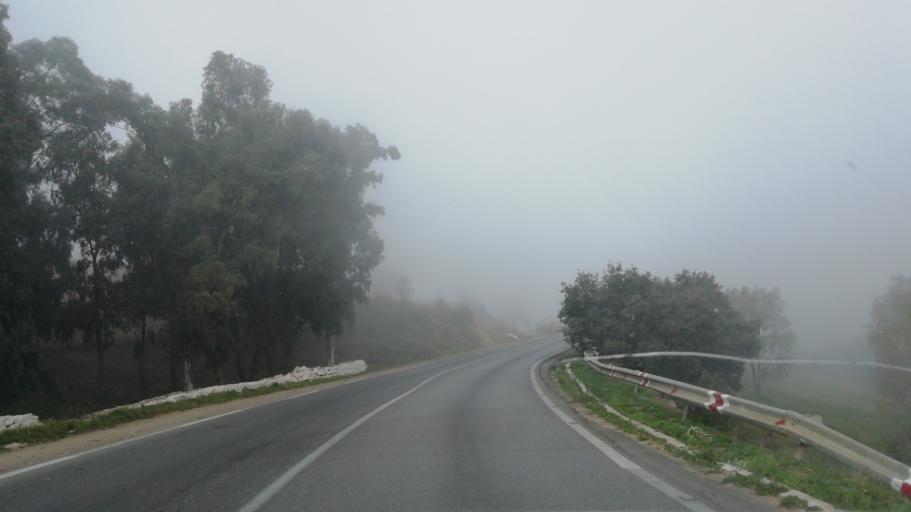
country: DZ
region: Mascara
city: Mascara
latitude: 35.5264
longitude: 0.3383
